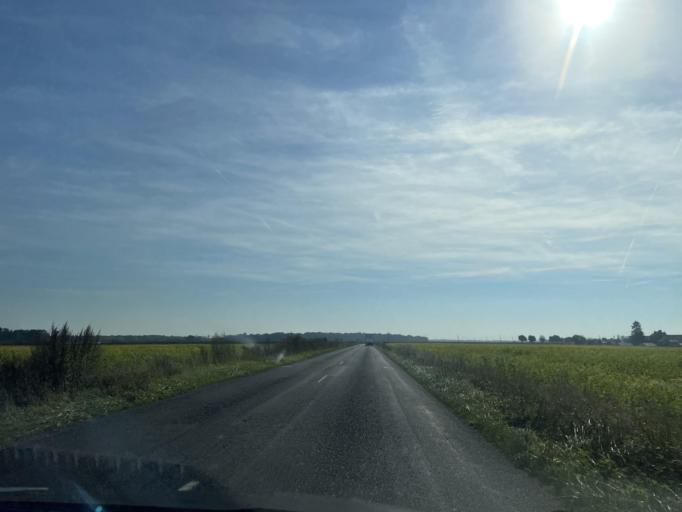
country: FR
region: Ile-de-France
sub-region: Departement de Seine-et-Marne
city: Coulommiers
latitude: 48.8713
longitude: 3.0876
